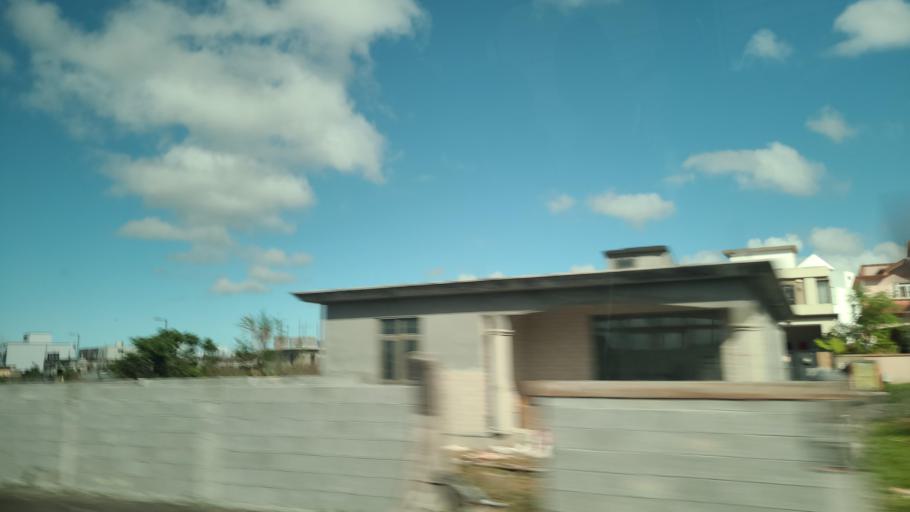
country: MU
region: Moka
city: Providence
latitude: -20.2462
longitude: 57.6099
